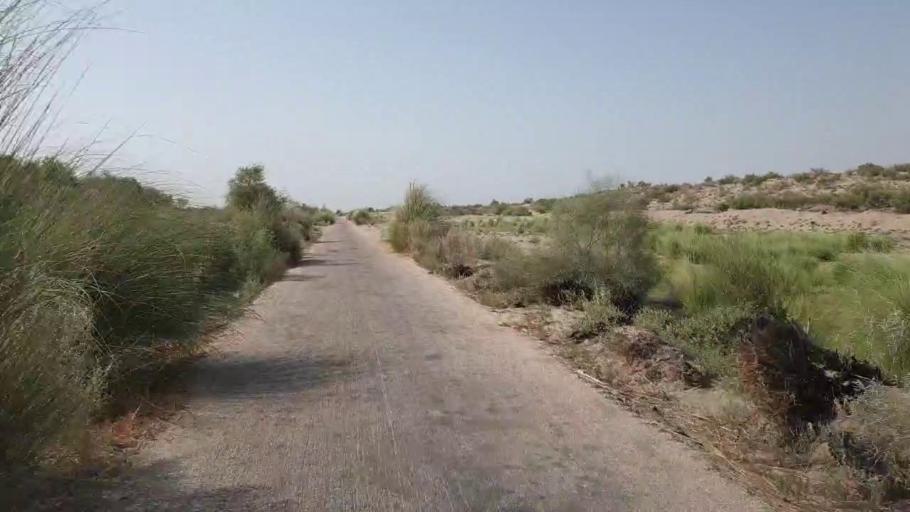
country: PK
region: Sindh
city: Jam Sahib
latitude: 26.5700
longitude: 68.9223
